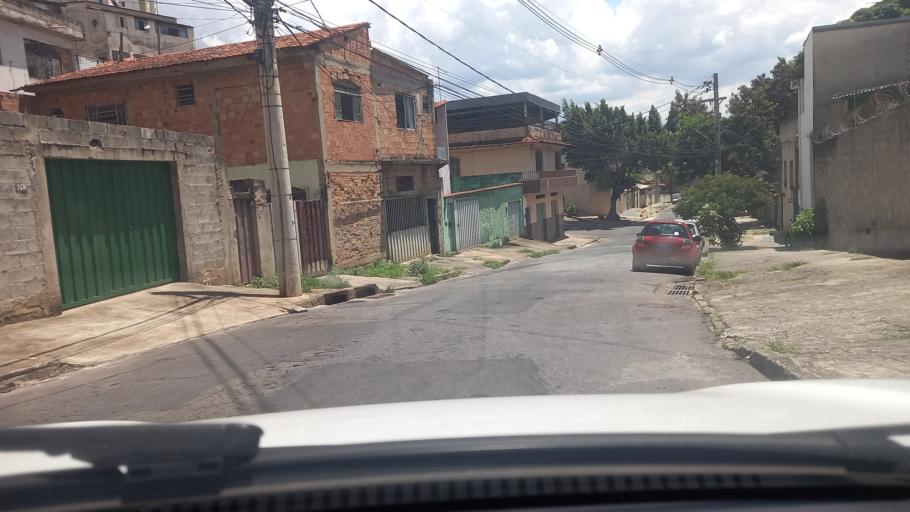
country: BR
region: Minas Gerais
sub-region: Belo Horizonte
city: Belo Horizonte
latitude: -19.9171
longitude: -43.9831
